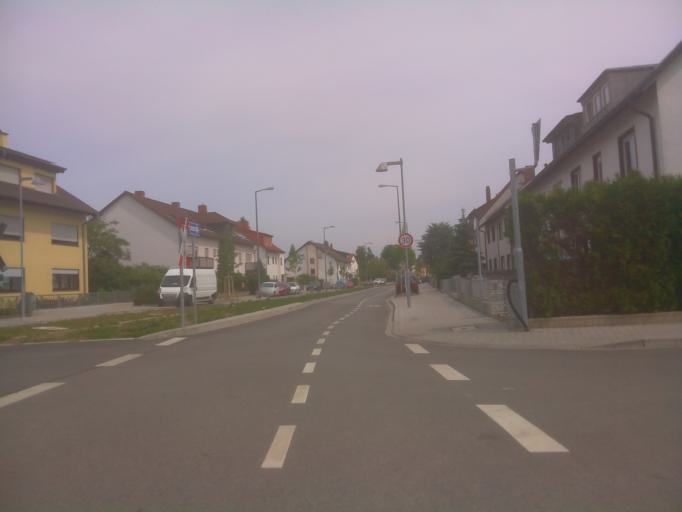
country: DE
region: Baden-Wuerttemberg
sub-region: Karlsruhe Region
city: Mannheim
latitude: 49.5160
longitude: 8.4966
